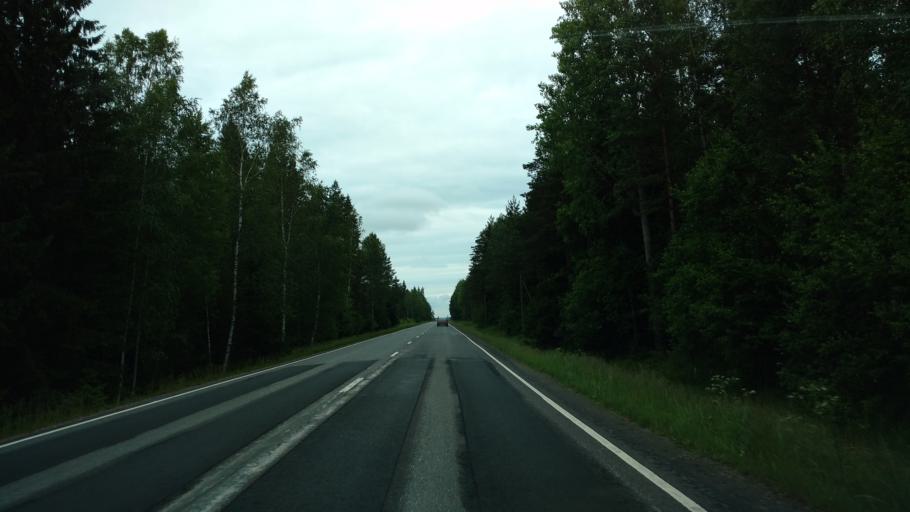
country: FI
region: Varsinais-Suomi
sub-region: Salo
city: Halikko
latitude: 60.4565
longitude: 23.0238
